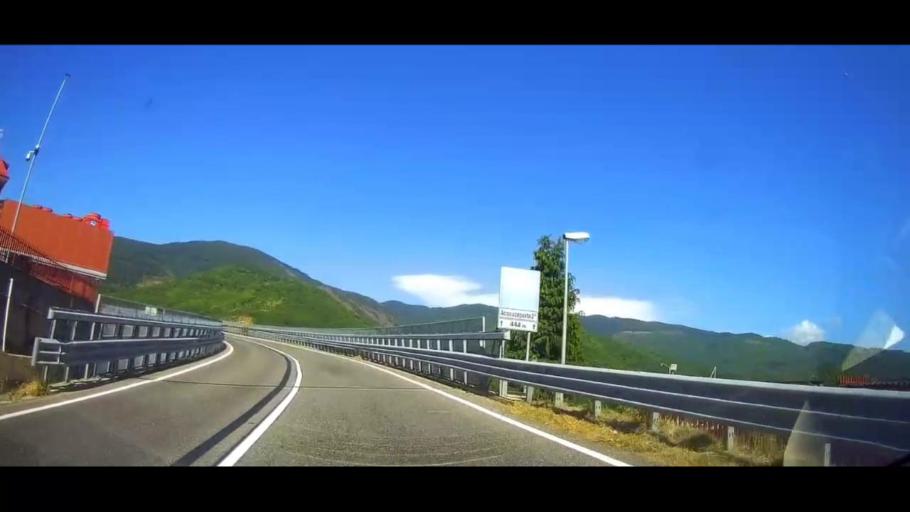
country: IT
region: Calabria
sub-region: Provincia di Cosenza
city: Spezzano Piccolo
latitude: 39.2930
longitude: 16.3452
